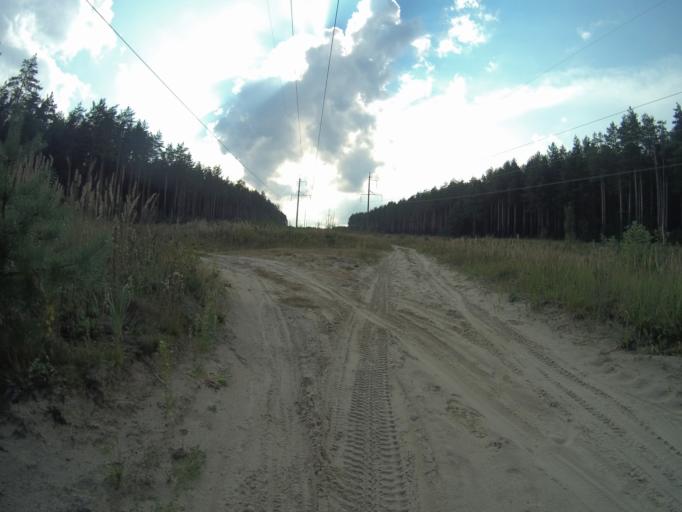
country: RU
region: Vladimir
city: Raduzhnyy
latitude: 56.0164
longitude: 40.3022
